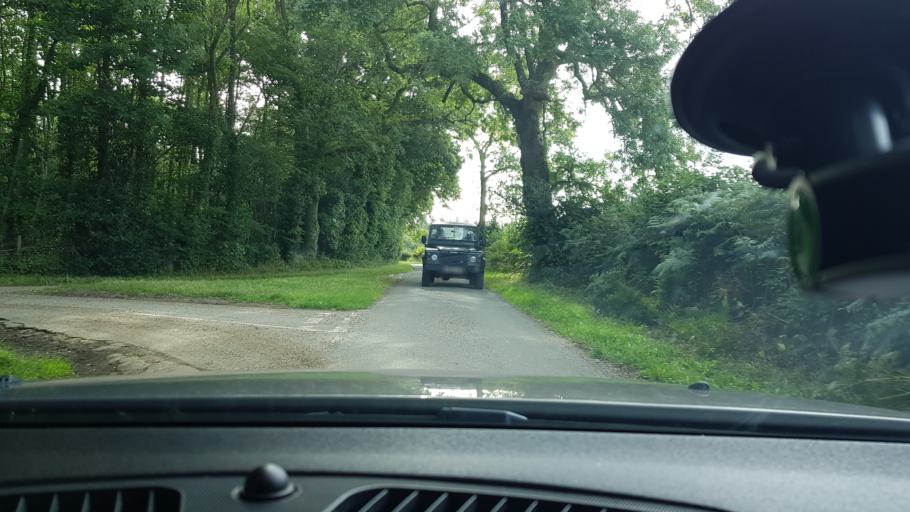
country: GB
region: England
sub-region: Wiltshire
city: Chilton Foliat
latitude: 51.4619
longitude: -1.5376
